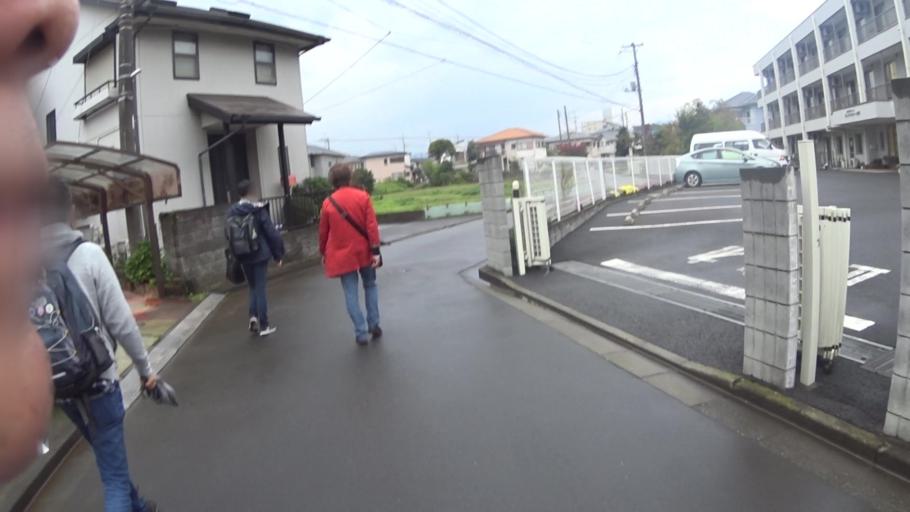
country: JP
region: Kanagawa
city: Hadano
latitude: 35.3676
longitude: 139.2166
